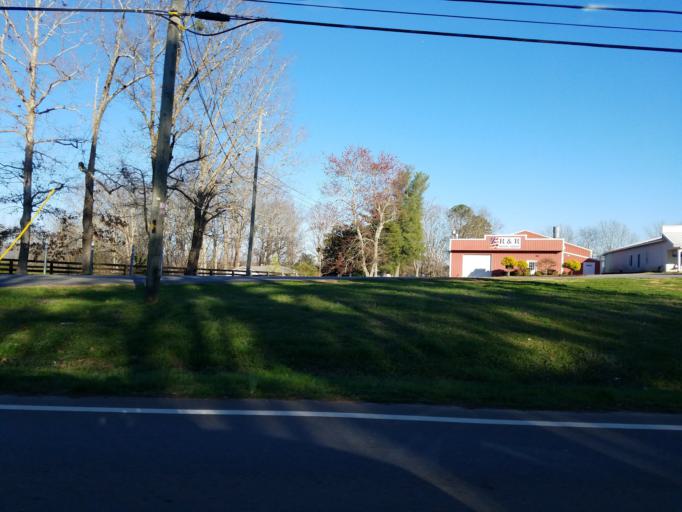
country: US
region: Georgia
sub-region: Pickens County
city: Jasper
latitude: 34.4234
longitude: -84.4192
